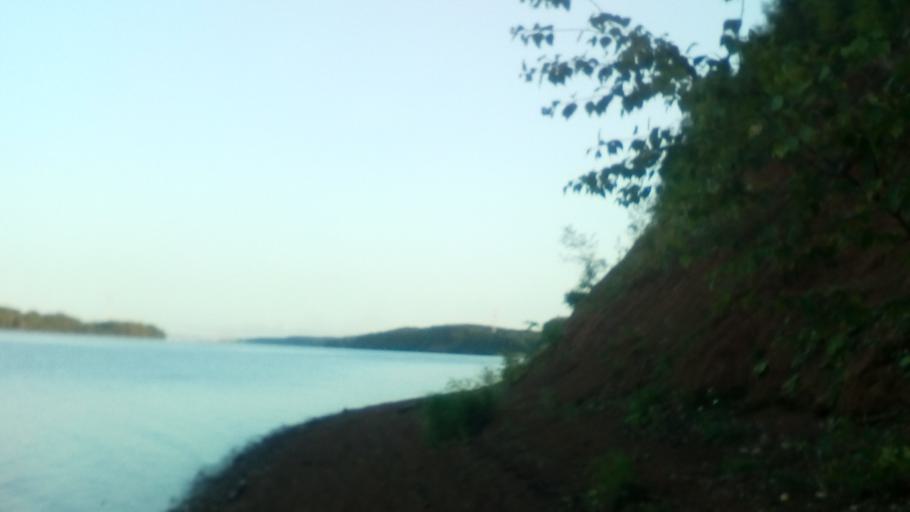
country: RU
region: Perm
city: Usol'ye
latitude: 59.4878
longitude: 56.5864
